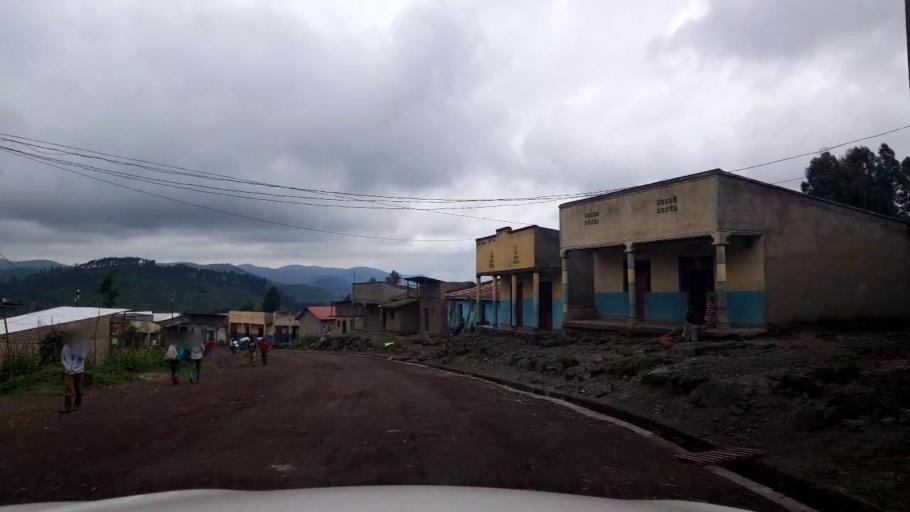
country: RW
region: Northern Province
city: Musanze
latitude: -1.6023
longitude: 29.4516
